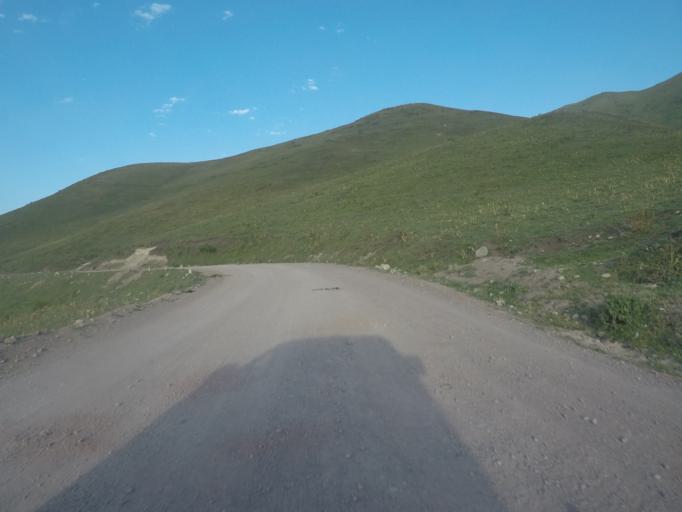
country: KG
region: Chuy
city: Bishkek
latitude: 42.6401
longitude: 74.6408
